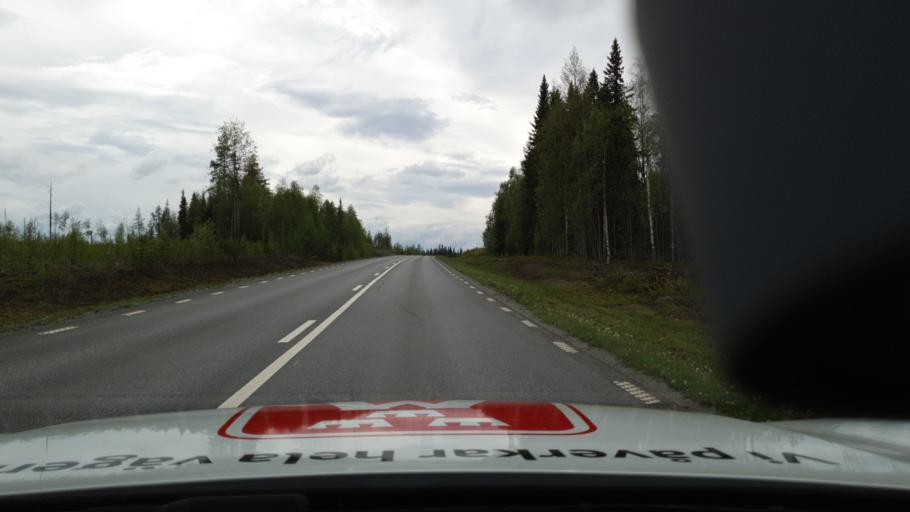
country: SE
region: Vaesterbotten
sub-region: Vilhelmina Kommun
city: Vilhelmina
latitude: 64.4119
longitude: 16.7394
